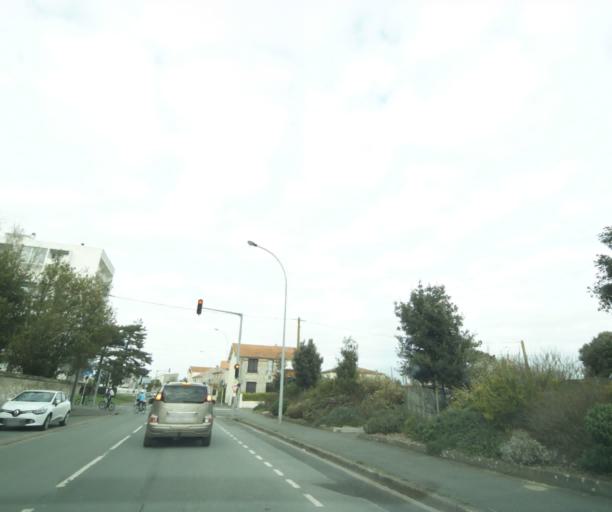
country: FR
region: Poitou-Charentes
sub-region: Departement de la Charente-Maritime
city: La Rochelle
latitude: 46.1664
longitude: -1.1641
